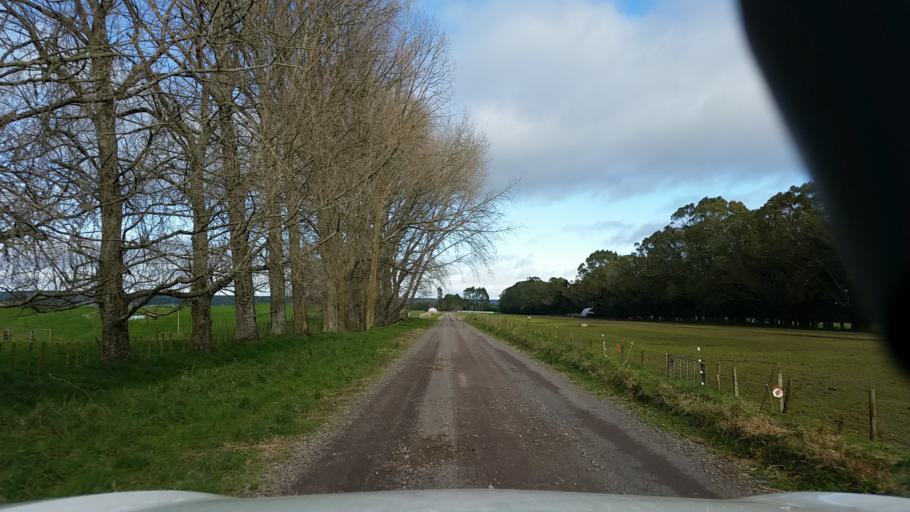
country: NZ
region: Bay of Plenty
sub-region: Whakatane District
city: Murupara
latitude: -38.4712
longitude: 176.4168
